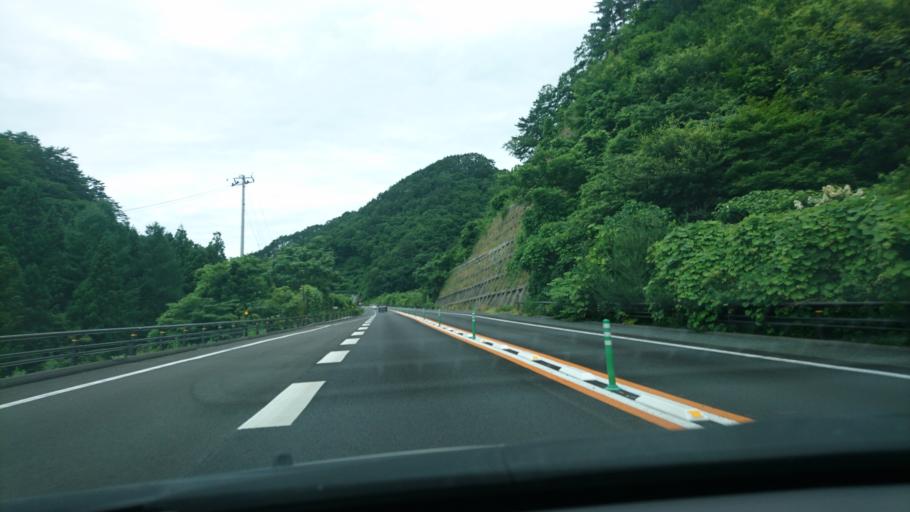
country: JP
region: Iwate
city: Miyako
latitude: 39.8450
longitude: 141.9523
